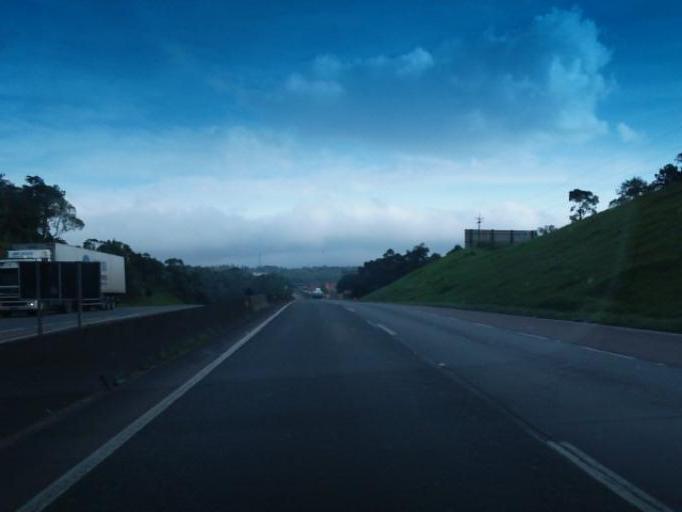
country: BR
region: Parana
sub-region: Sao Jose Dos Pinhais
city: Sao Jose dos Pinhais
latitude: -25.7619
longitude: -49.1251
